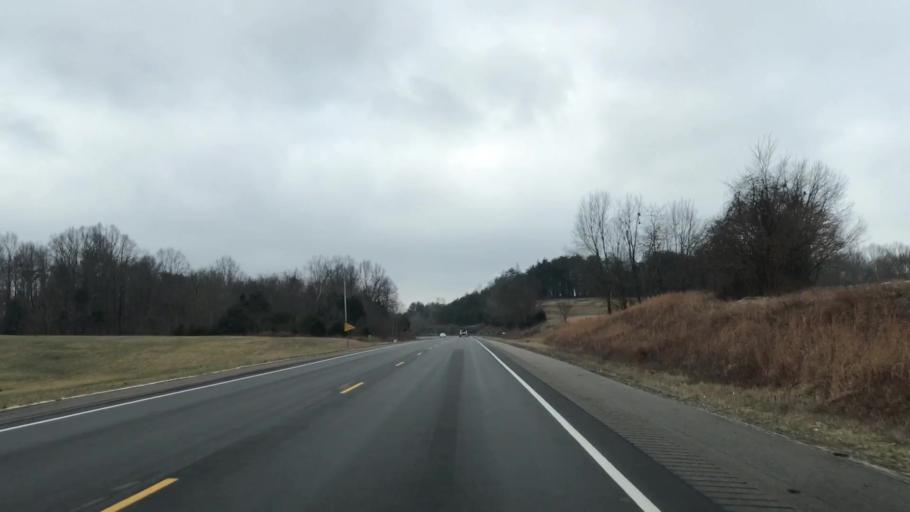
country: US
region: Kentucky
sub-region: Metcalfe County
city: Edmonton
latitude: 36.9533
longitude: -85.4430
